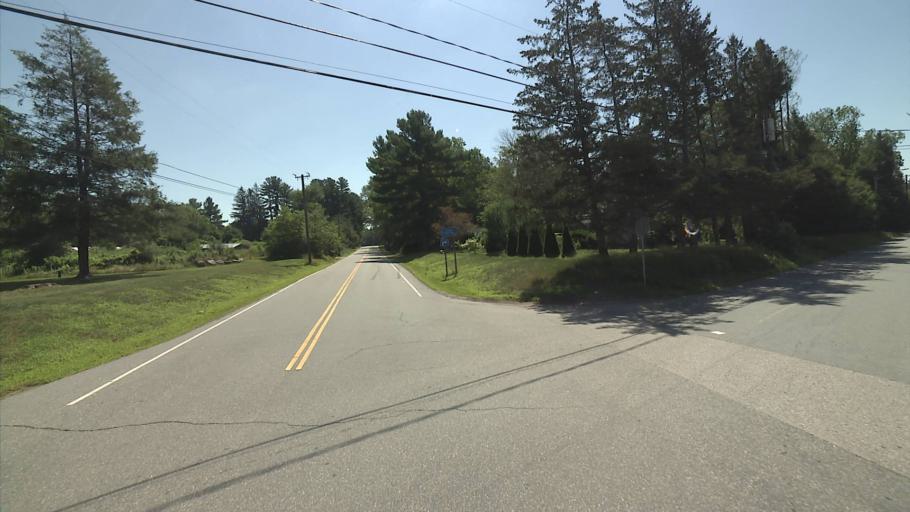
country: US
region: Connecticut
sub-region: Windham County
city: Moosup
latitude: 41.6993
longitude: -71.7939
